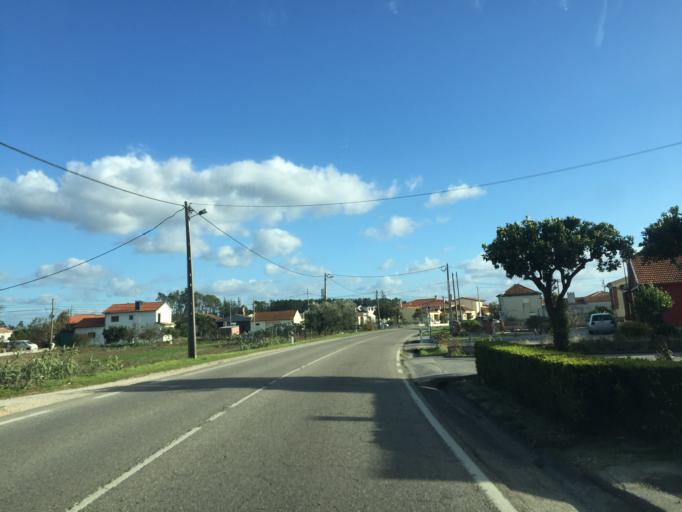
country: PT
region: Leiria
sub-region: Pombal
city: Lourical
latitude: 39.9719
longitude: -8.7936
